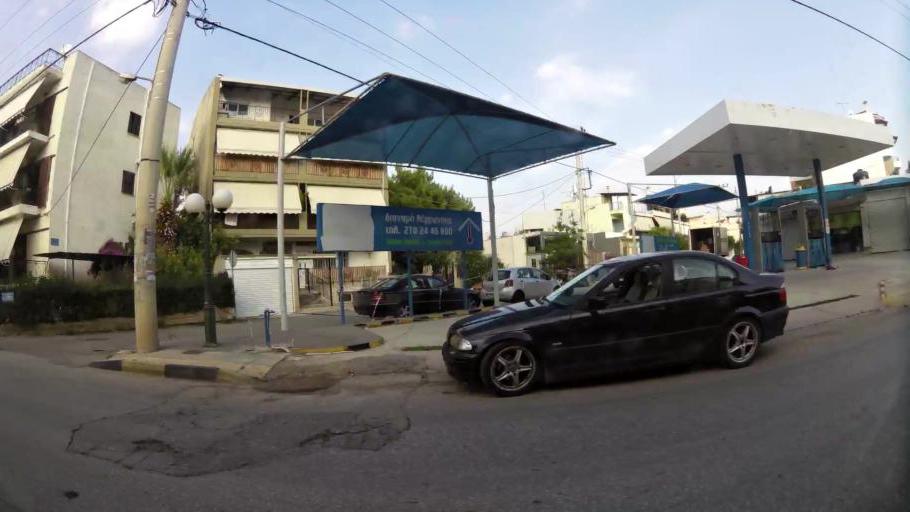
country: GR
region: Attica
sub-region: Nomarchia Anatolikis Attikis
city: Acharnes
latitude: 38.0882
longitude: 23.7439
